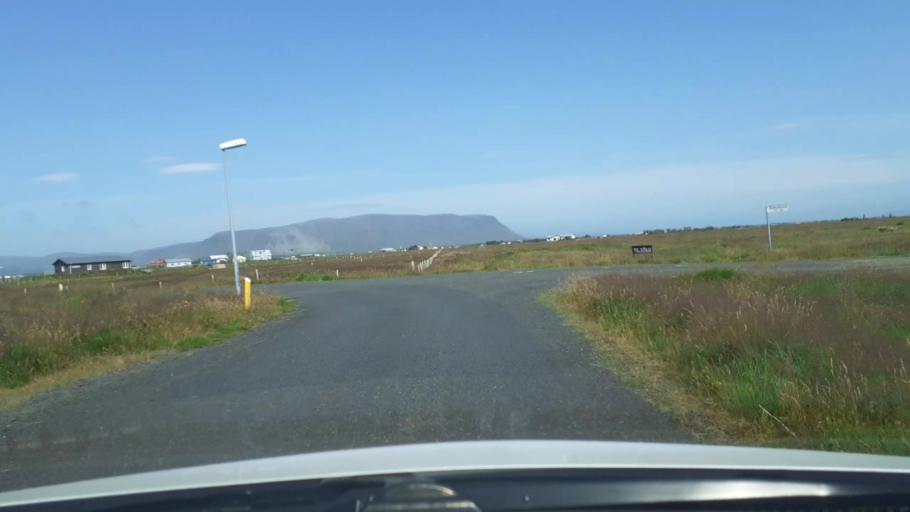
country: IS
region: South
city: Selfoss
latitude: 63.8904
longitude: -21.0853
